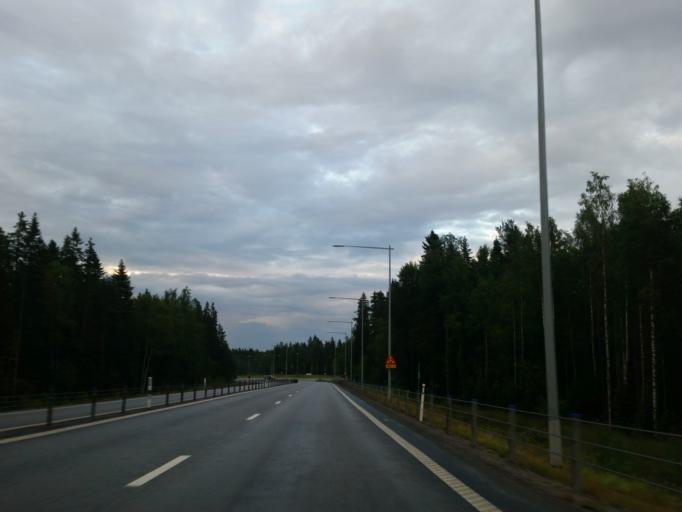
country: SE
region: Vaesterbotten
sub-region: Umea Kommun
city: Ersmark
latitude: 63.8474
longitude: 20.3352
